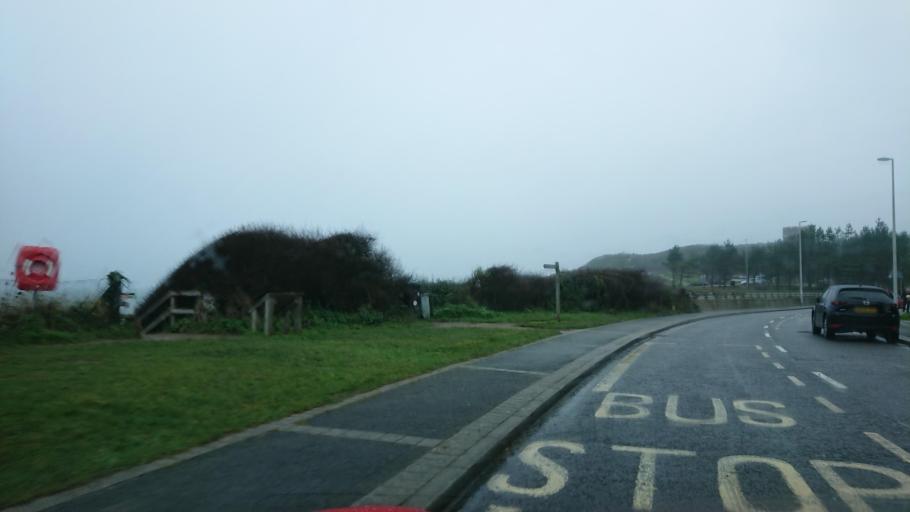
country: GB
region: England
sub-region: Plymouth
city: Plymouth
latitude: 50.3576
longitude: -4.1259
